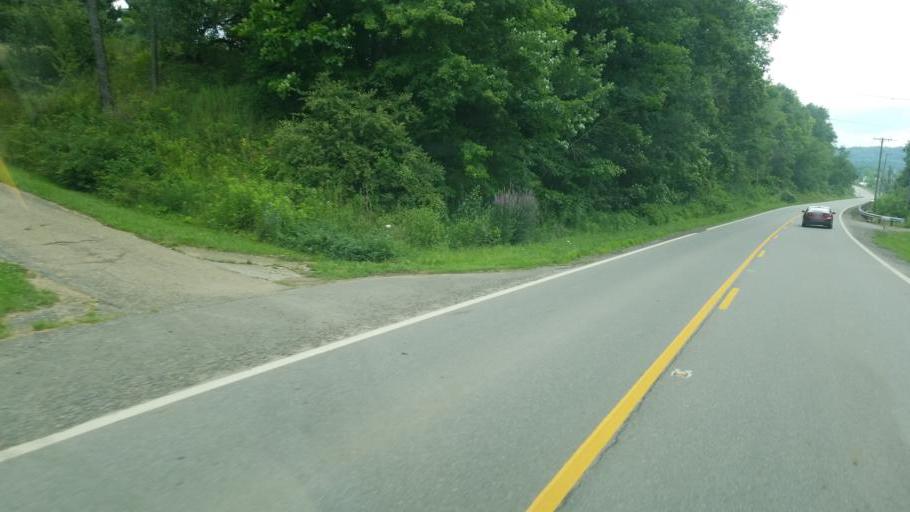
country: US
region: Ohio
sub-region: Columbiana County
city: Lisbon
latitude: 40.7634
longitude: -80.7818
